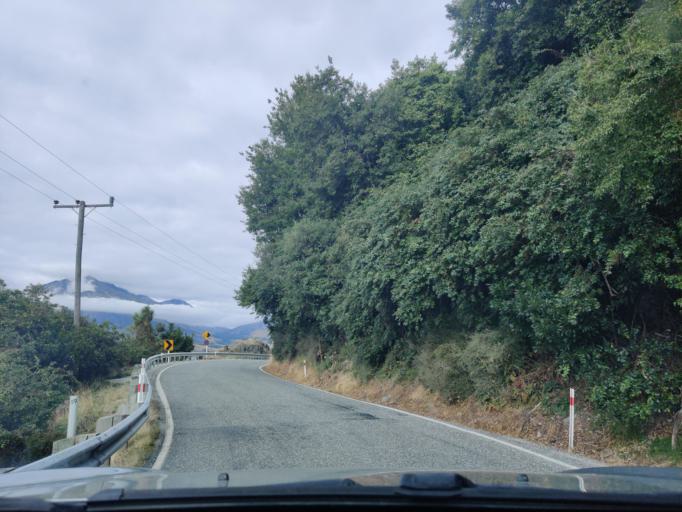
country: NZ
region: Otago
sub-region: Queenstown-Lakes District
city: Queenstown
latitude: -45.0777
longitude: 168.4880
